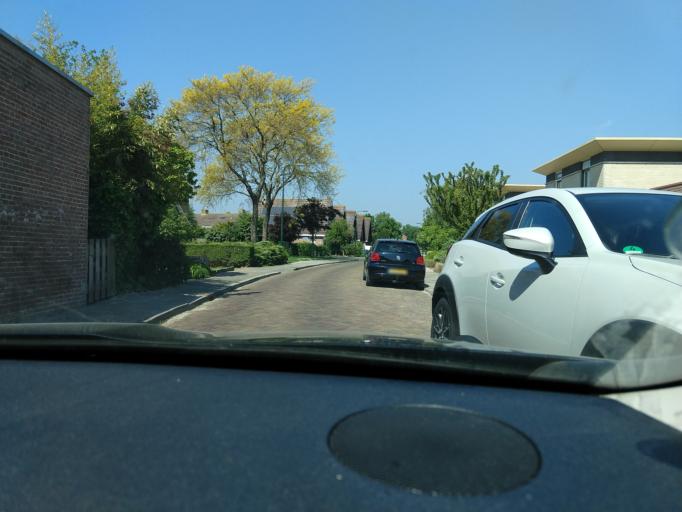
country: NL
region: Zeeland
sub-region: Gemeente Reimerswaal
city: Yerseke
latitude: 51.5480
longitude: 4.0729
